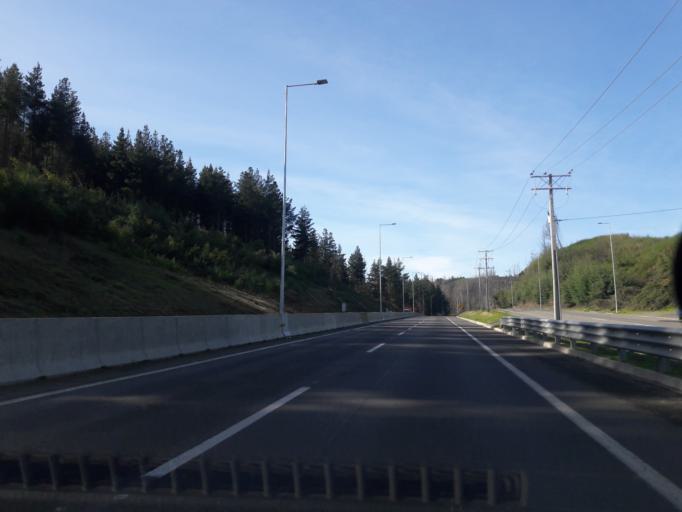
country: CL
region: Biobio
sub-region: Provincia de Concepcion
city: Penco
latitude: -36.8571
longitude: -72.8657
